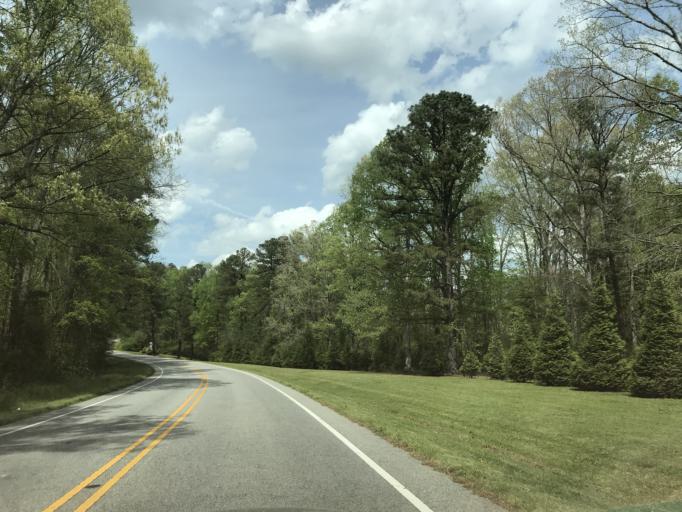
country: US
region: North Carolina
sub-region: Nash County
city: Spring Hope
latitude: 35.9683
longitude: -78.2092
